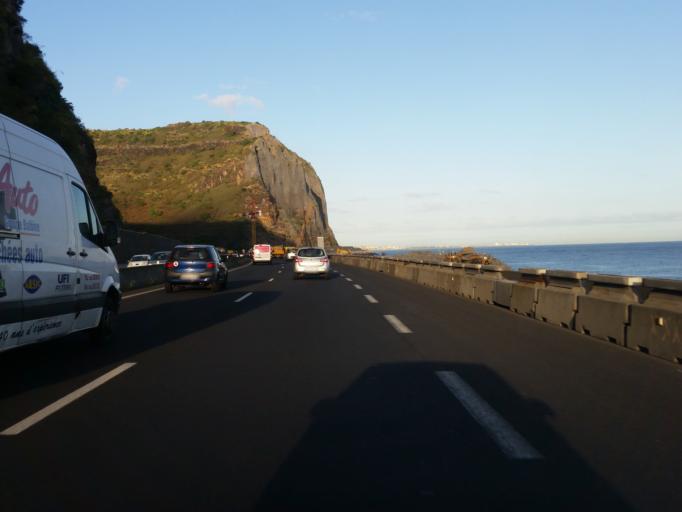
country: RE
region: Reunion
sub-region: Reunion
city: La Possession
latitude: -20.8926
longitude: 55.3800
